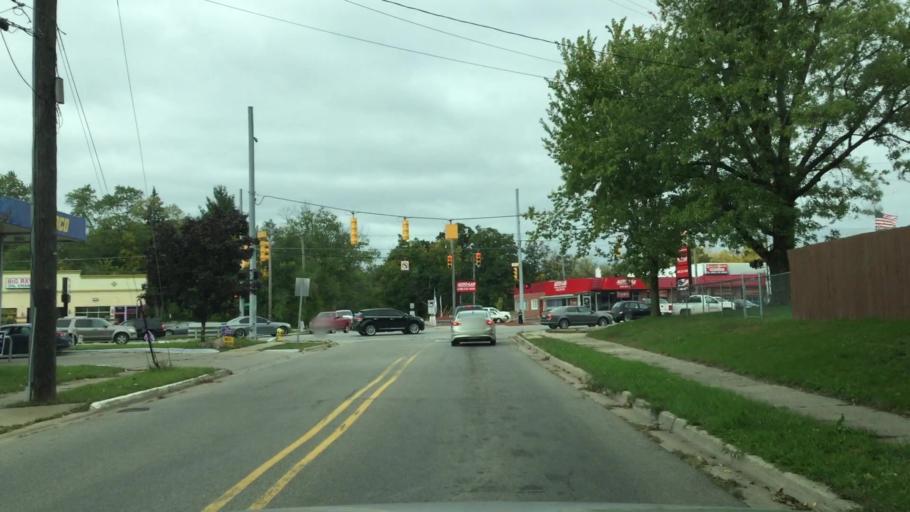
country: US
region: Michigan
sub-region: Oakland County
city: Sylvan Lake
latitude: 42.6294
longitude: -83.3246
